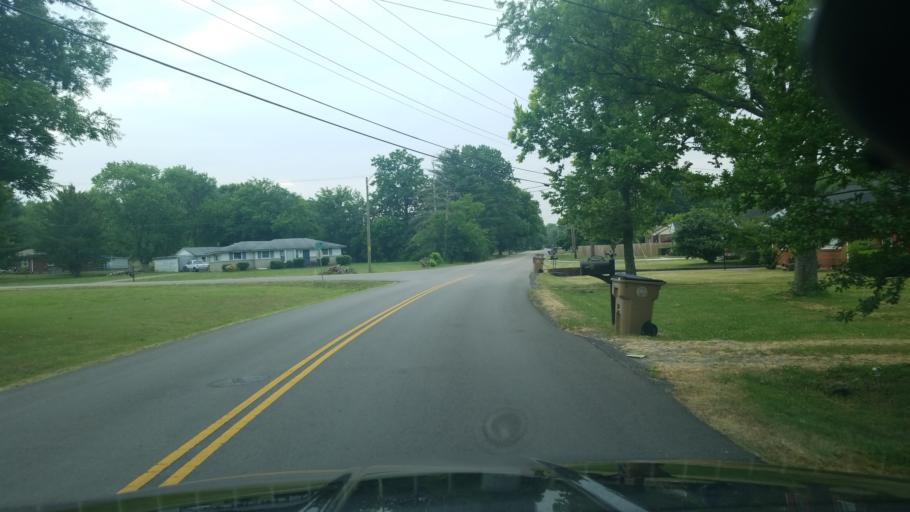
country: US
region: Tennessee
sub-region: Davidson County
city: Goodlettsville
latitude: 36.2657
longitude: -86.7484
